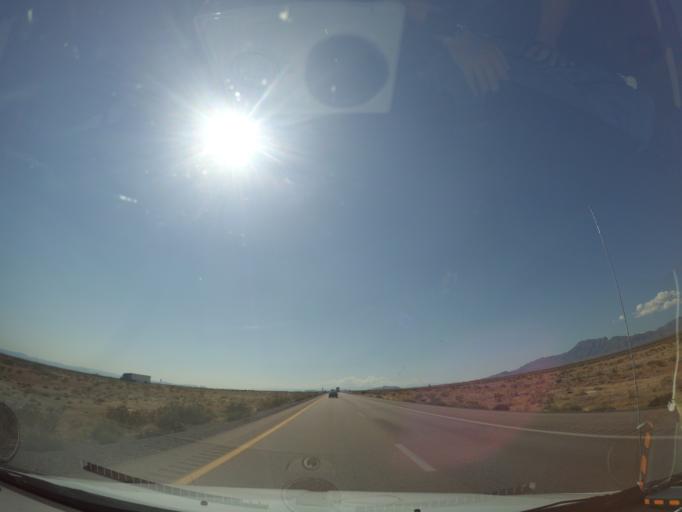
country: US
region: Nevada
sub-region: Clark County
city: Bunkerville
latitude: 36.7751
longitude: -114.2895
